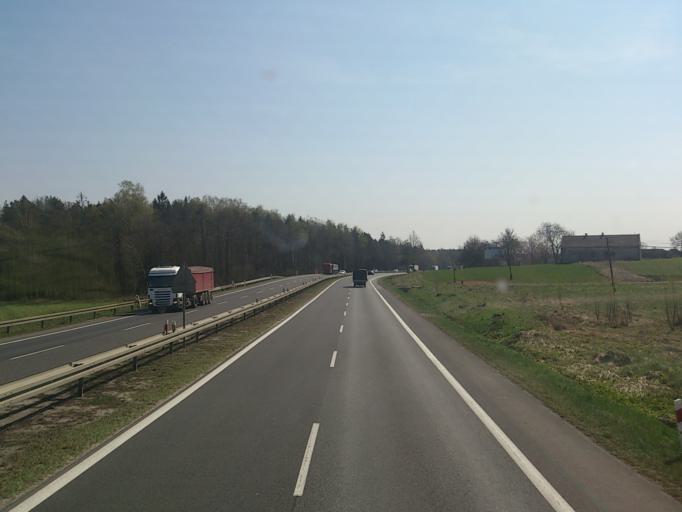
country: PL
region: Silesian Voivodeship
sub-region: Powiat myszkowski
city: Kozieglowy
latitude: 50.5486
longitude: 19.1800
